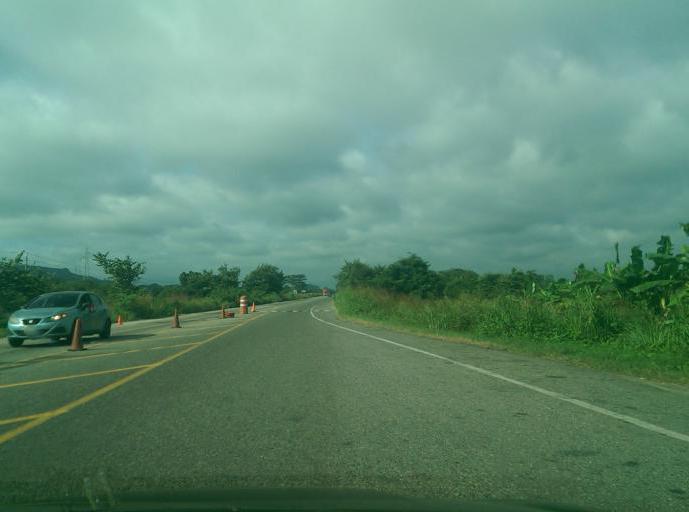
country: MX
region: Tabasco
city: Aquiles Serdan
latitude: 17.6931
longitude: -92.3161
